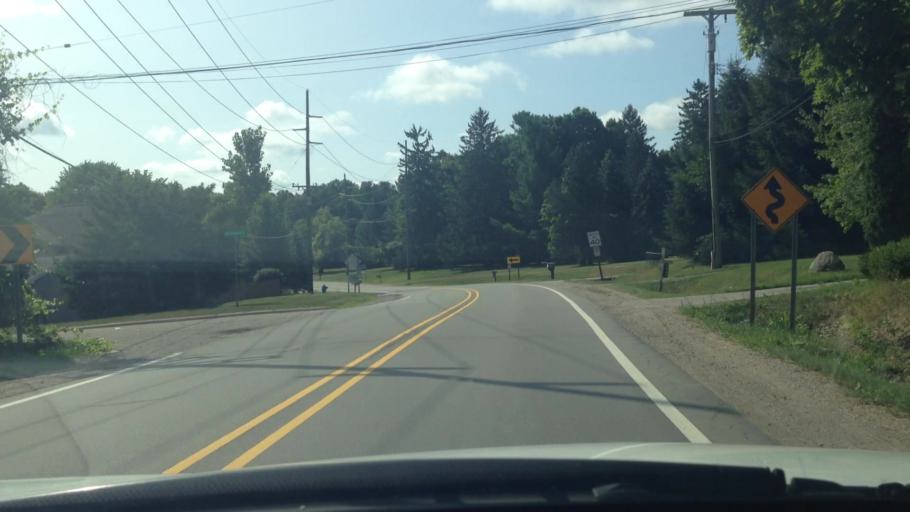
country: US
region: Michigan
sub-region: Oakland County
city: Waterford
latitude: 42.6915
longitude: -83.4398
